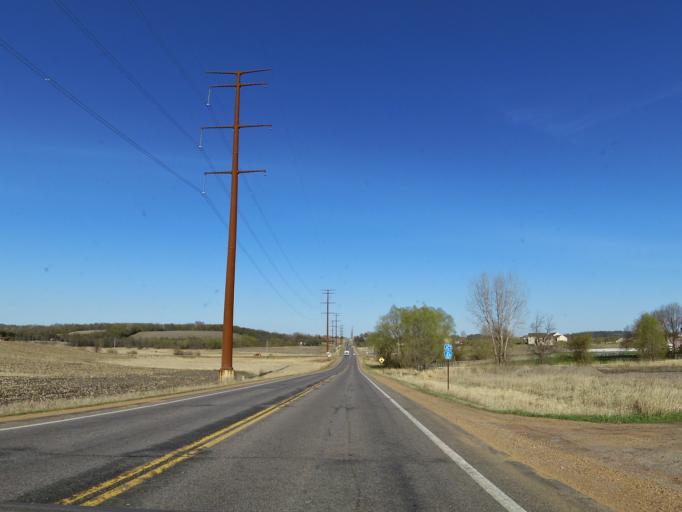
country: US
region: Minnesota
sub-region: Rice County
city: Lonsdale
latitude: 44.5726
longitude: -93.4441
